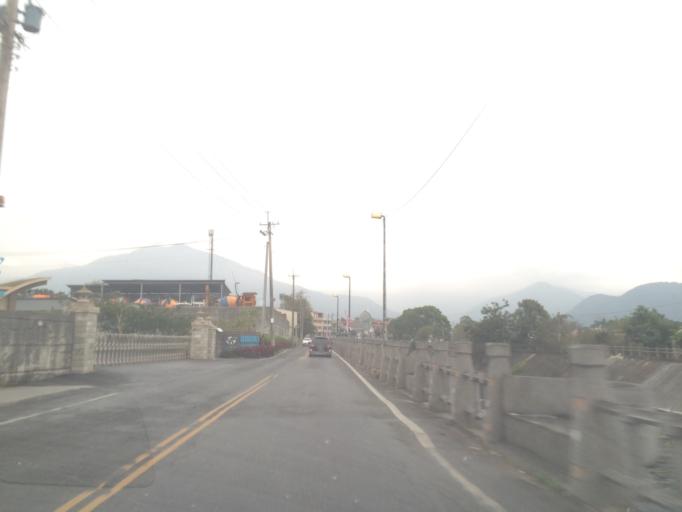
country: TW
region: Taiwan
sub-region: Nantou
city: Puli
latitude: 23.9648
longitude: 120.9570
